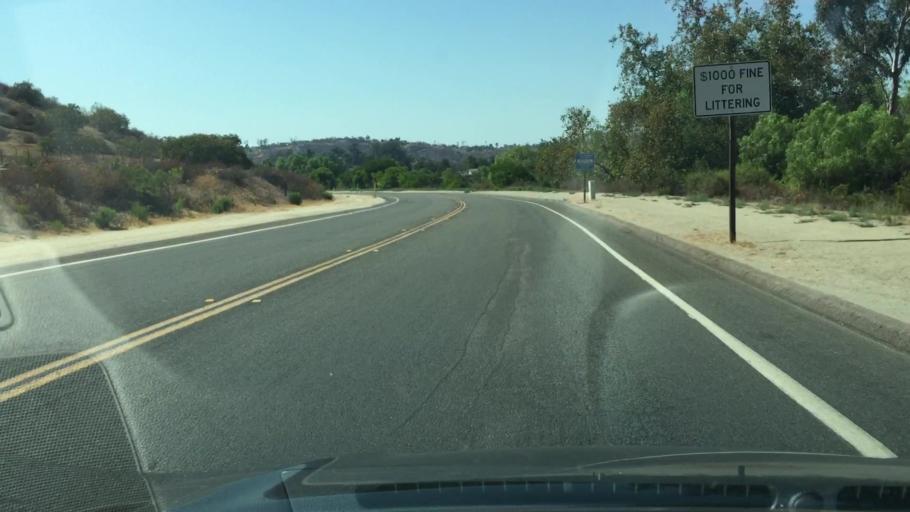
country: US
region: California
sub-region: San Diego County
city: Jamul
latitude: 32.7375
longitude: -116.8937
